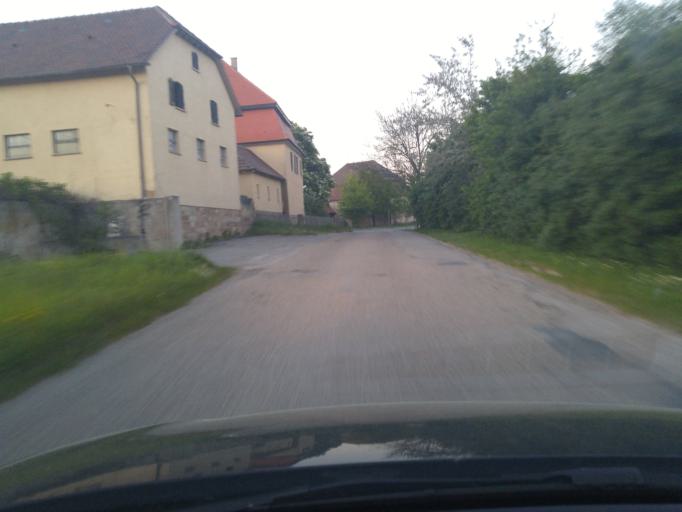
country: DE
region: Baden-Wuerttemberg
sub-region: Regierungsbezirk Stuttgart
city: Cleebronn
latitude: 49.0396
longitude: 9.0538
